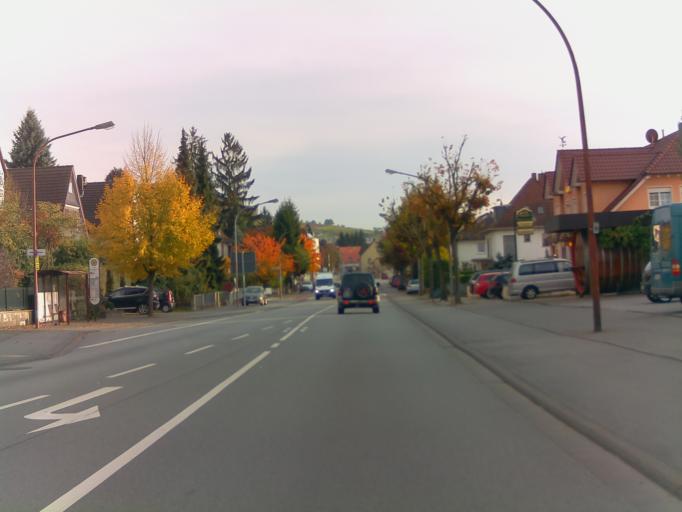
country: DE
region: Hesse
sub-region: Regierungsbezirk Darmstadt
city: Heppenheim an der Bergstrasse
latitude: 49.6485
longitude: 8.6386
